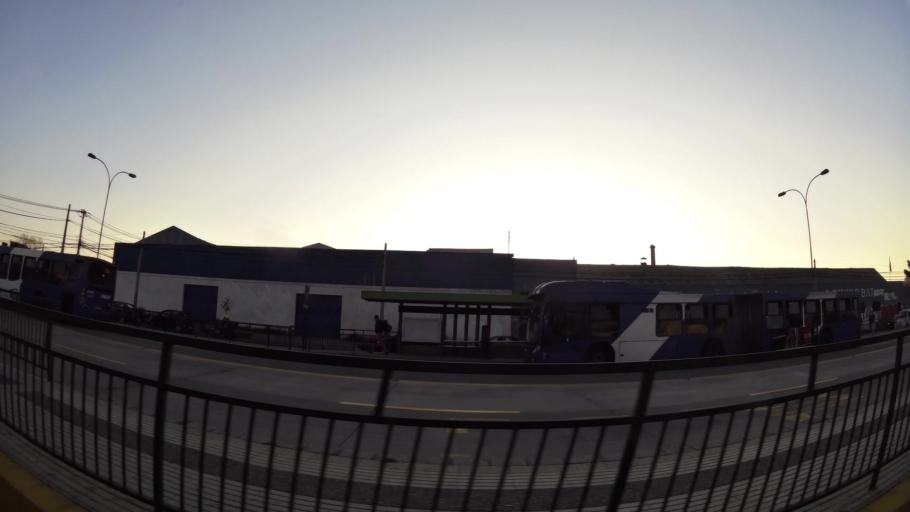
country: CL
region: Santiago Metropolitan
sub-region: Provincia de Santiago
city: Santiago
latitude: -33.4915
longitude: -70.6403
